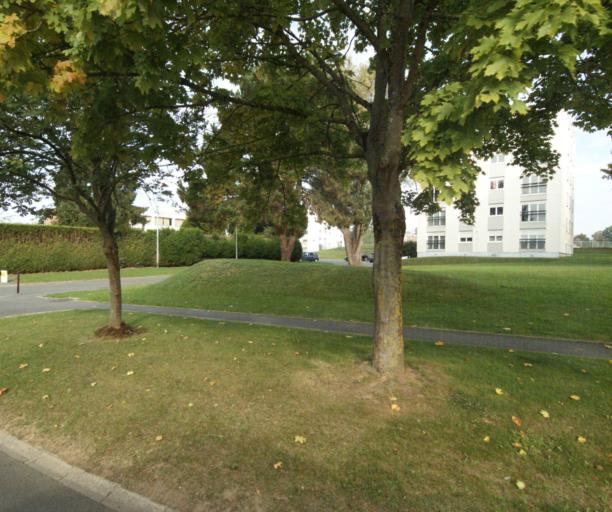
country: FR
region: Nord-Pas-de-Calais
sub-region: Departement du Nord
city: Wattignies
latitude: 50.5854
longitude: 3.0394
